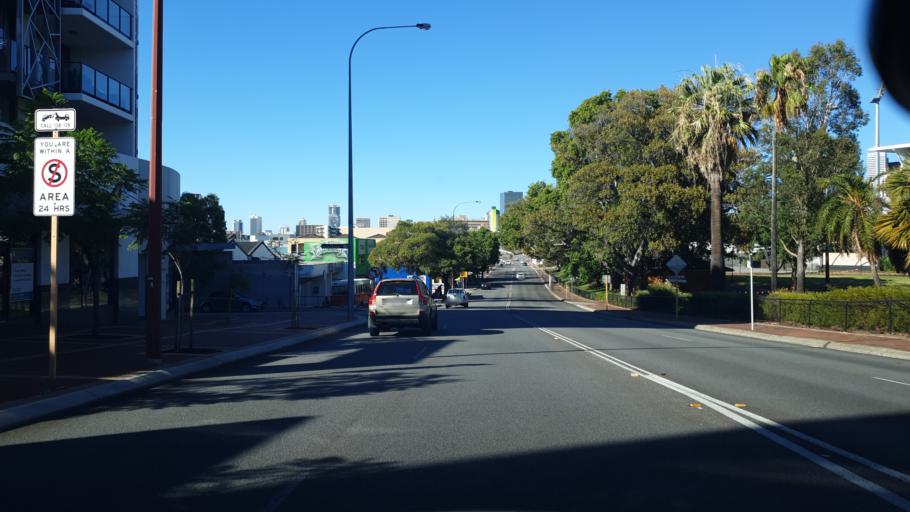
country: AU
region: Western Australia
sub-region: Vincent
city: Mount Lawley
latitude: -31.9454
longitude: 115.8724
